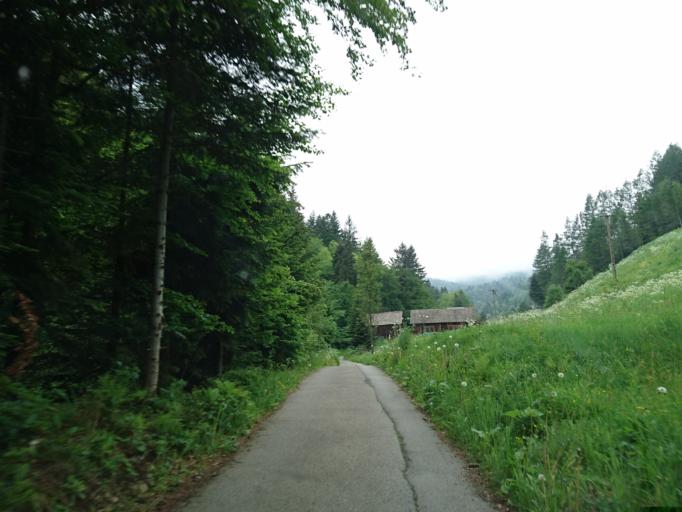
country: PL
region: Lesser Poland Voivodeship
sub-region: Powiat limanowski
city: Lubomierz
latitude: 49.5349
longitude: 20.2053
